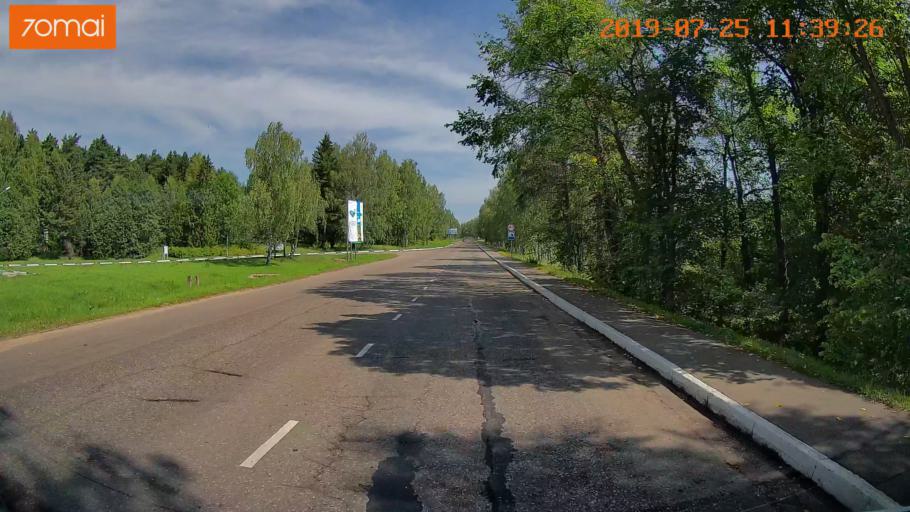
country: RU
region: Ivanovo
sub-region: Privolzhskiy Rayon
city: Ples
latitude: 57.4488
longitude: 41.4971
